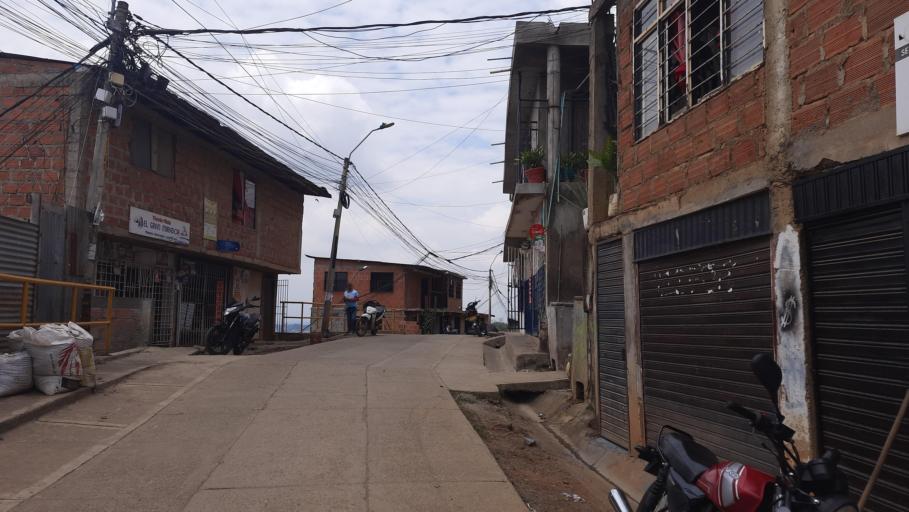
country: CO
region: Valle del Cauca
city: Cali
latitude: 3.3779
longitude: -76.5584
